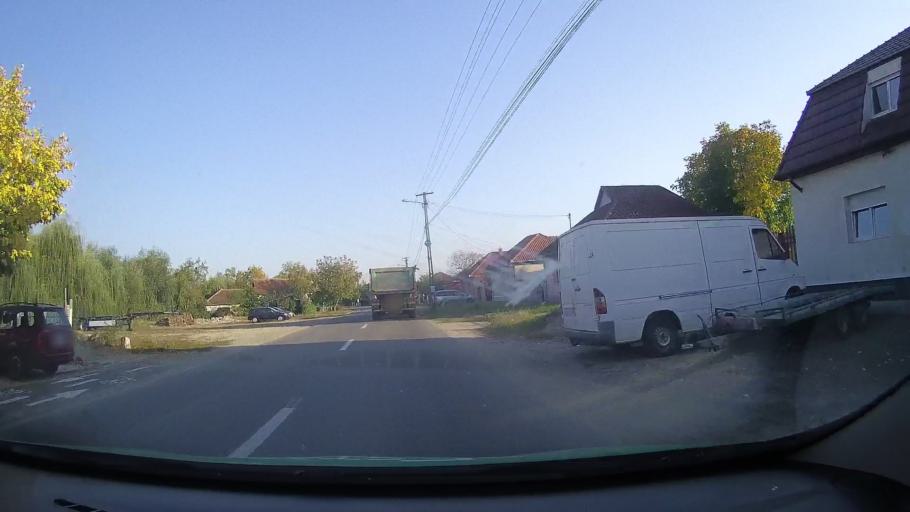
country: RO
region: Arad
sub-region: Comuna Pancota
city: Pancota
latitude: 46.3185
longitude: 21.6951
